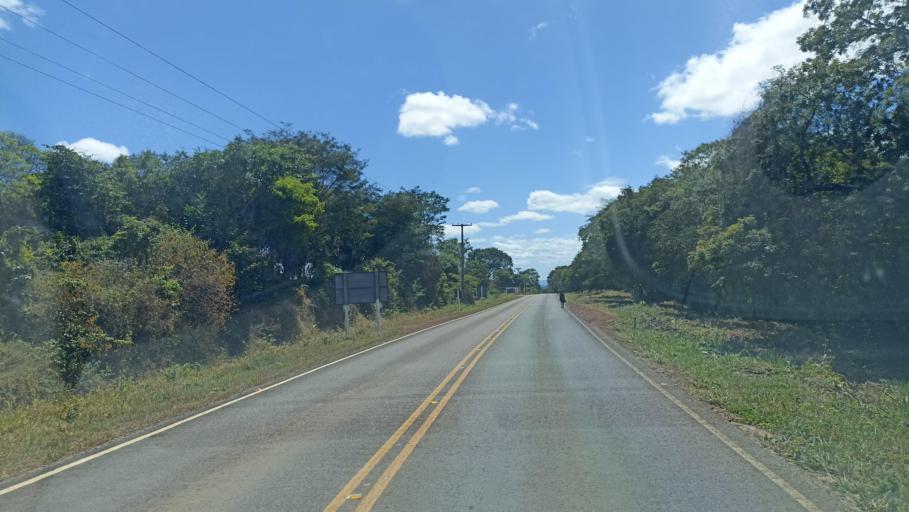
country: BR
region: Bahia
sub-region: Andarai
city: Vera Cruz
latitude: -12.7905
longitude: -41.3286
